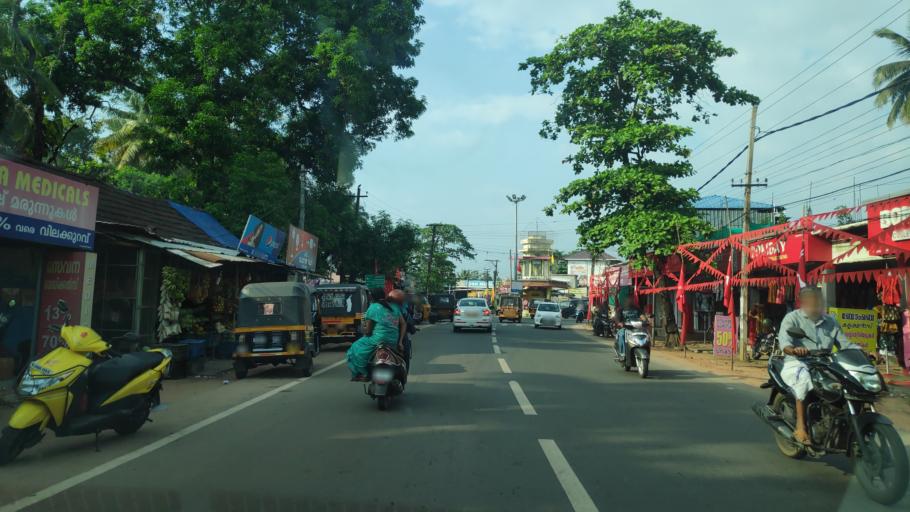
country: IN
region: Kerala
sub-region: Alappuzha
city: Alleppey
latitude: 9.5132
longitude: 76.3381
